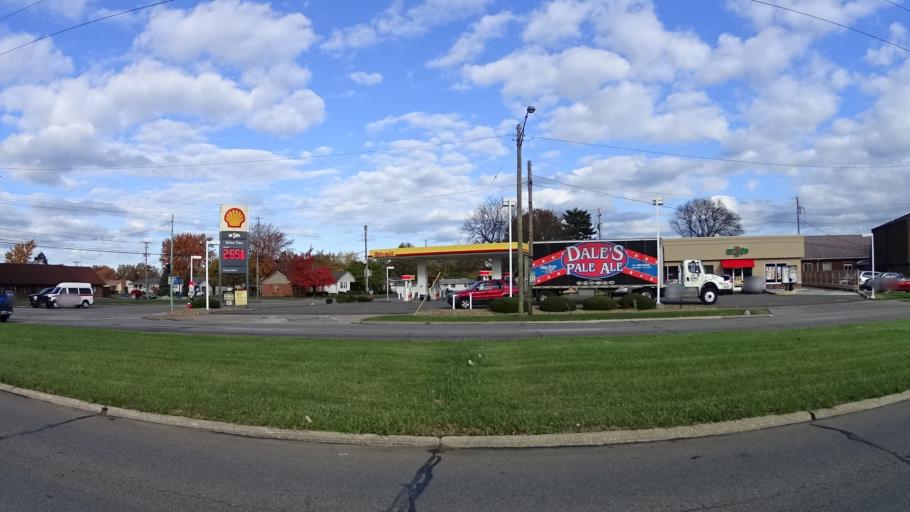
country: US
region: Ohio
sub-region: Lorain County
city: Lorain
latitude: 41.4337
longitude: -82.1850
